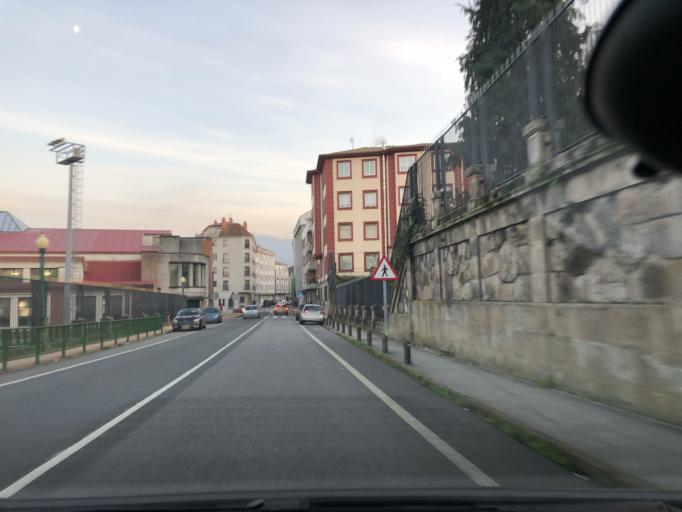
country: ES
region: Galicia
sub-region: Provincia de Pontevedra
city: Marin
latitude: 42.3940
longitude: -8.7070
